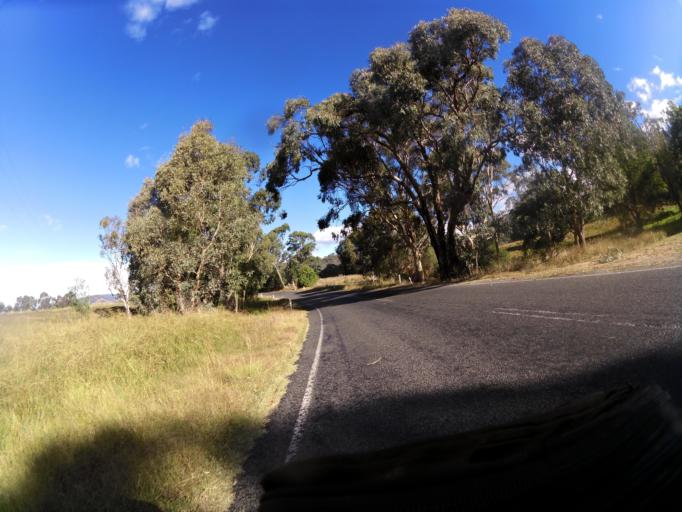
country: AU
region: New South Wales
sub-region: Greater Hume Shire
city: Holbrook
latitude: -35.9474
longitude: 147.7137
